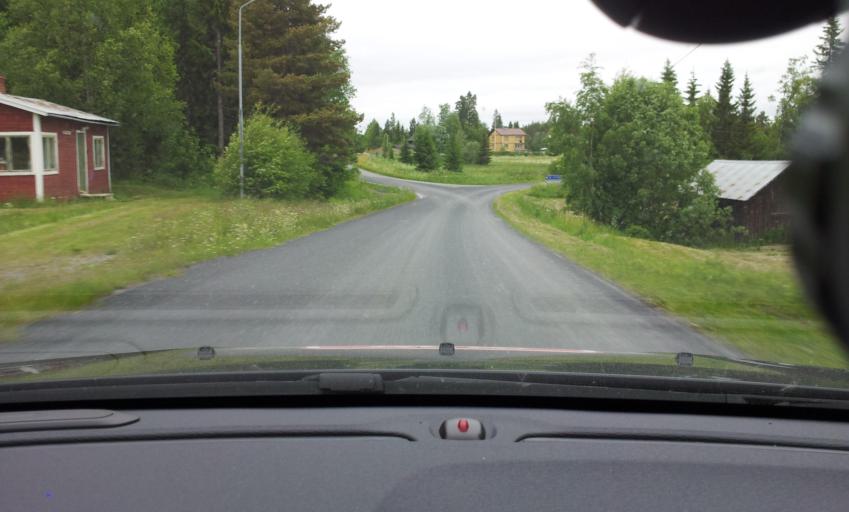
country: SE
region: Jaemtland
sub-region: Krokoms Kommun
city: Valla
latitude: 63.2694
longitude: 13.9013
